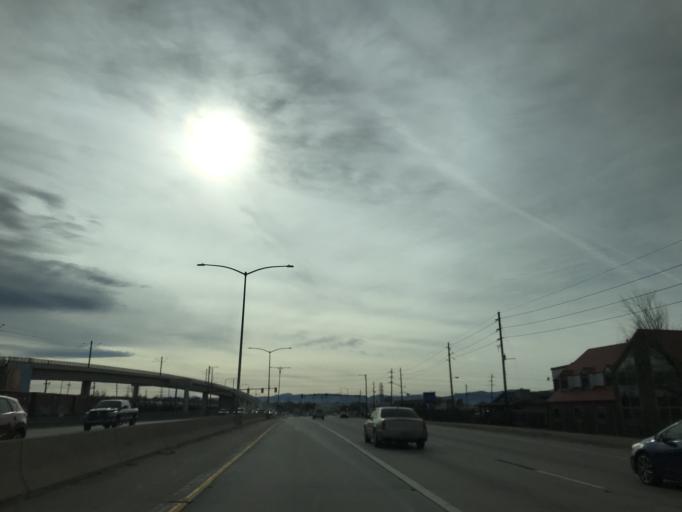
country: US
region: Colorado
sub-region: Arapahoe County
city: Sheridan
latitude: 39.6339
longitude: -105.0083
